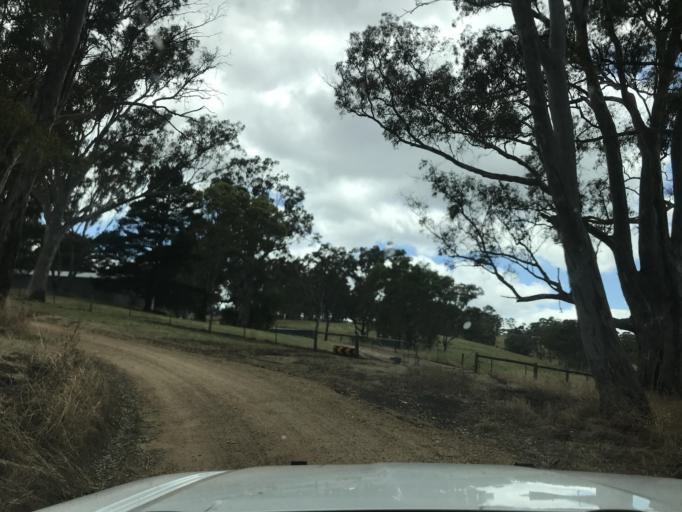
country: AU
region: South Australia
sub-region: Wattle Range
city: Penola
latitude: -37.3667
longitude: 141.2442
